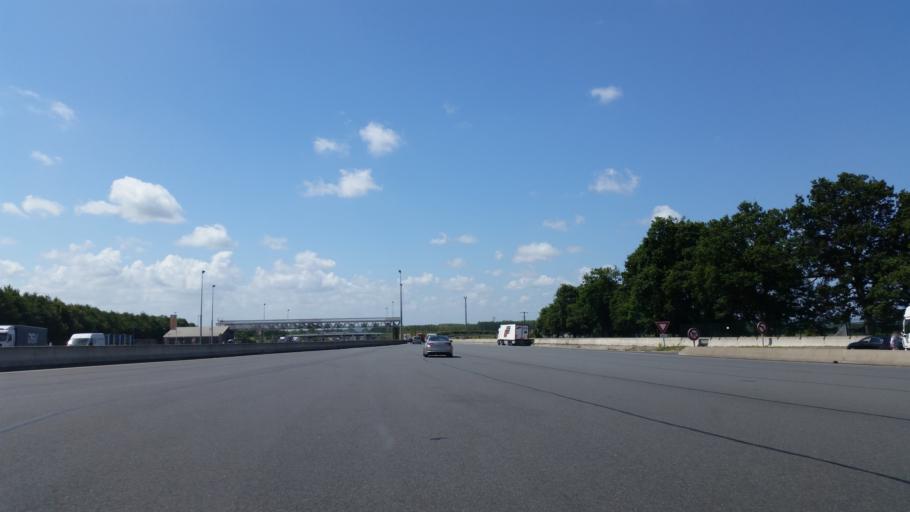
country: FR
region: Lower Normandy
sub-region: Departement du Calvados
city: Dozule
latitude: 49.2308
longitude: -0.0731
